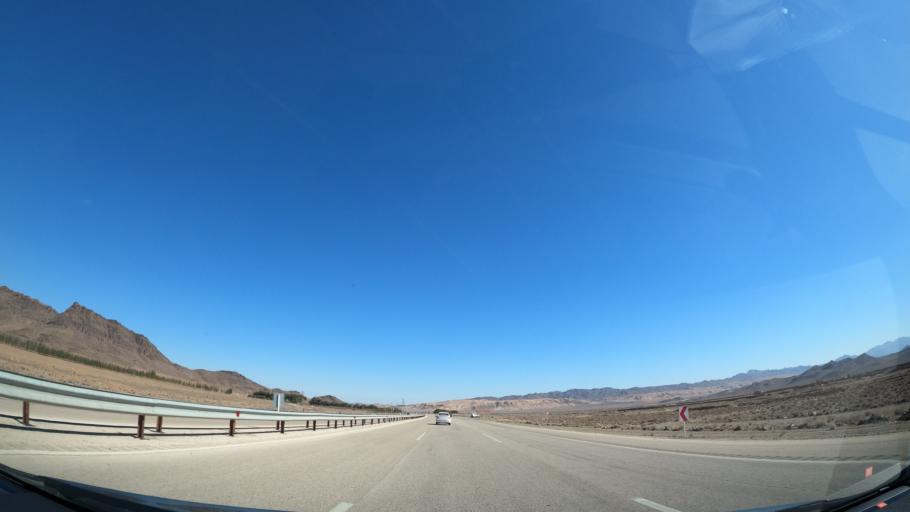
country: IR
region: Isfahan
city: Natanz
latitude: 33.3954
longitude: 51.9690
